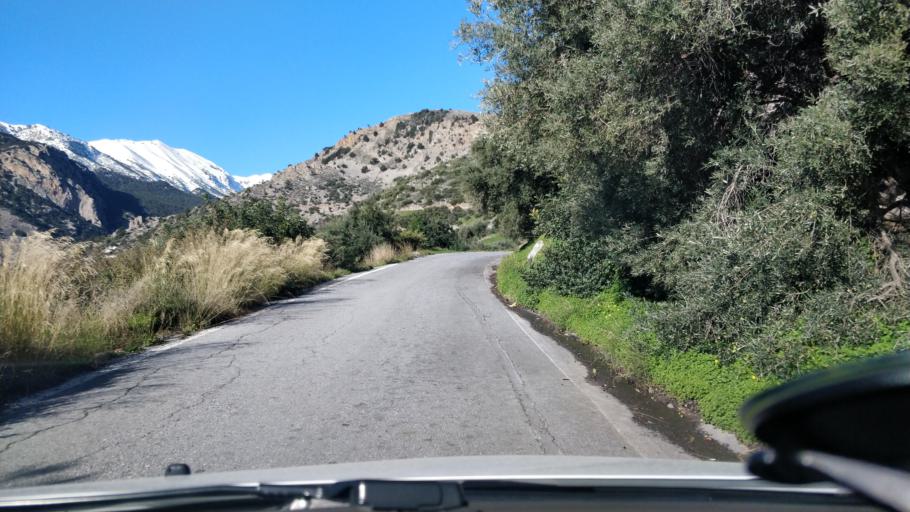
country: GR
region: Crete
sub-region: Nomos Lasithiou
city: Kritsa
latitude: 35.0773
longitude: 25.5836
